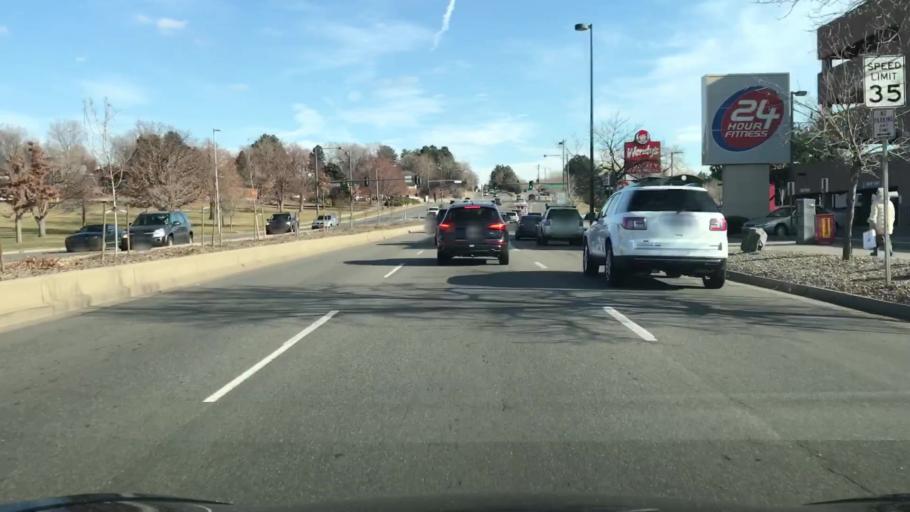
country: US
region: Colorado
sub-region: Arapahoe County
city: Glendale
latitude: 39.7114
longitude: -104.9397
